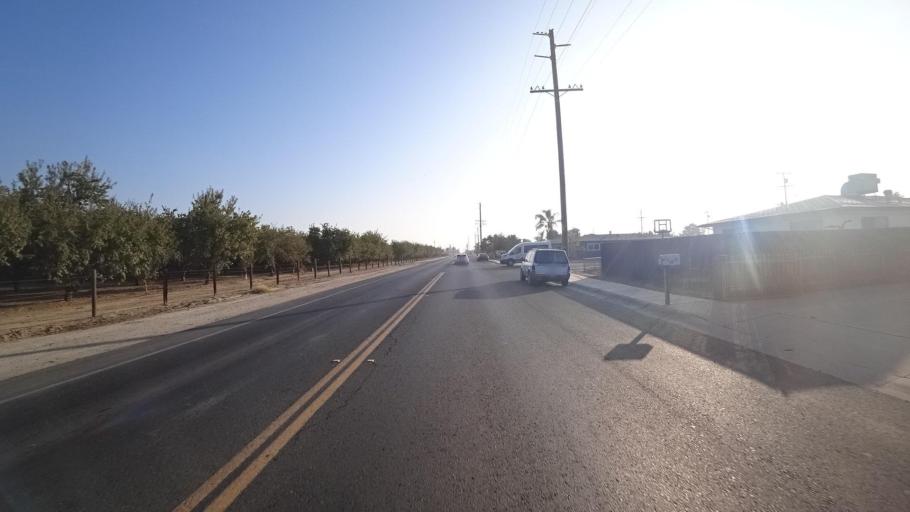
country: US
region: California
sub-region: Kern County
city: Delano
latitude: 35.7913
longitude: -119.2362
